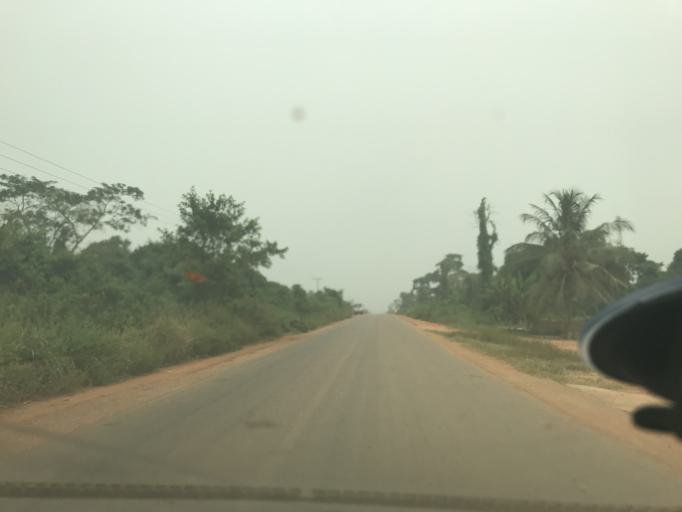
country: NG
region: Ogun
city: Owode
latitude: 6.8873
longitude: 3.5075
